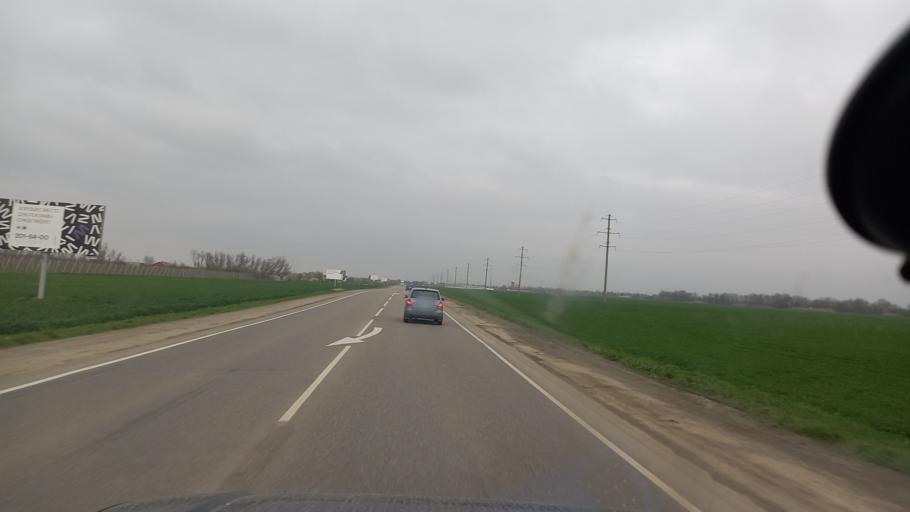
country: RU
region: Krasnodarskiy
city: Slavyansk-na-Kubani
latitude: 45.2454
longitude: 38.0503
